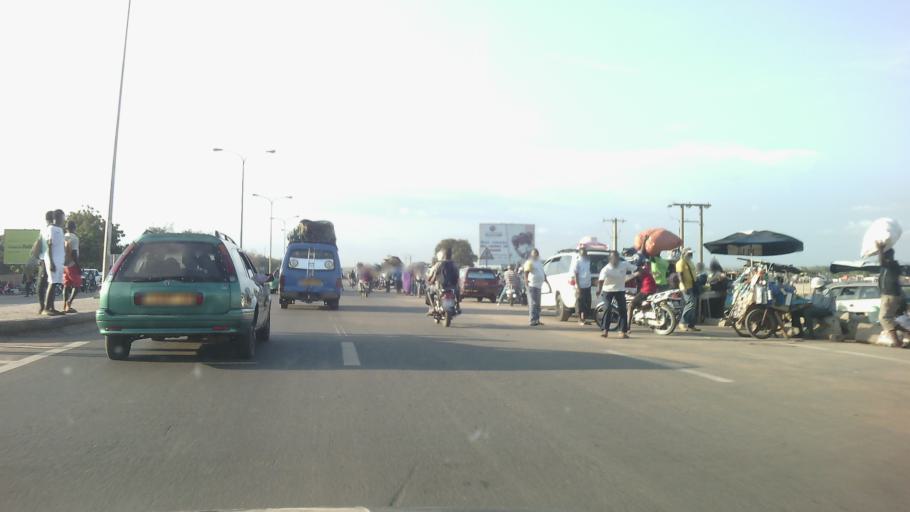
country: TG
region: Maritime
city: Lome
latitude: 6.2400
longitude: 1.2103
